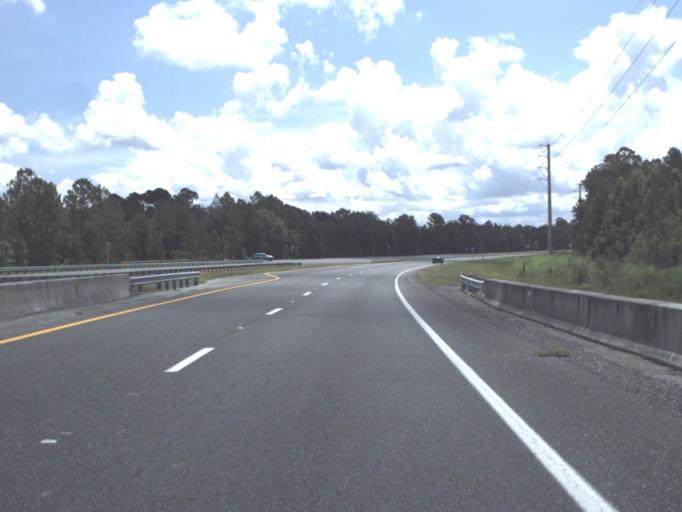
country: US
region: Florida
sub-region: Levy County
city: Bronson
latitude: 29.4766
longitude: -82.6869
